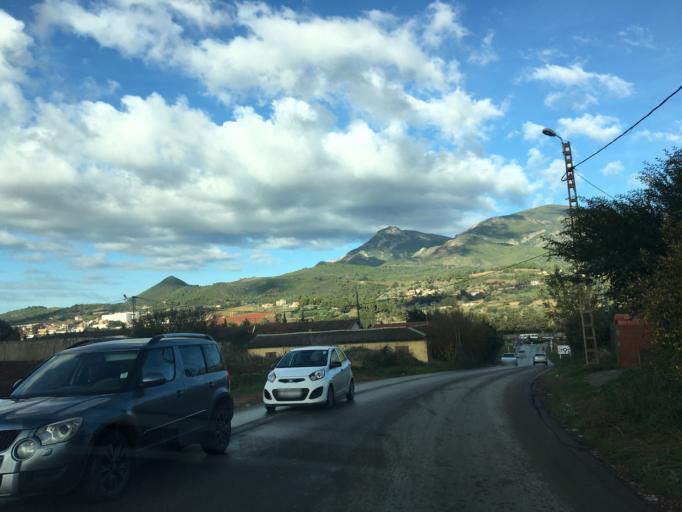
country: DZ
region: Tipaza
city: Tipasa
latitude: 36.5704
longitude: 2.4068
